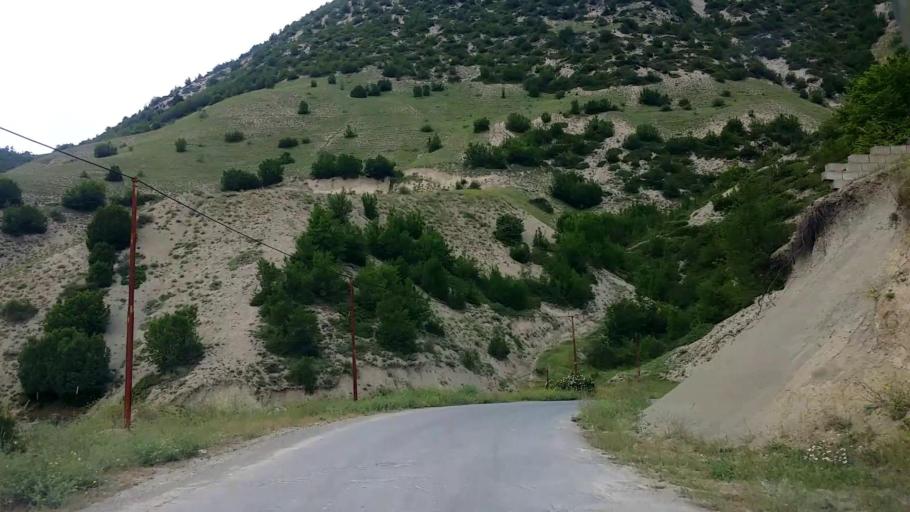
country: IR
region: Mazandaran
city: Chalus
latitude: 36.5531
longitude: 51.2801
